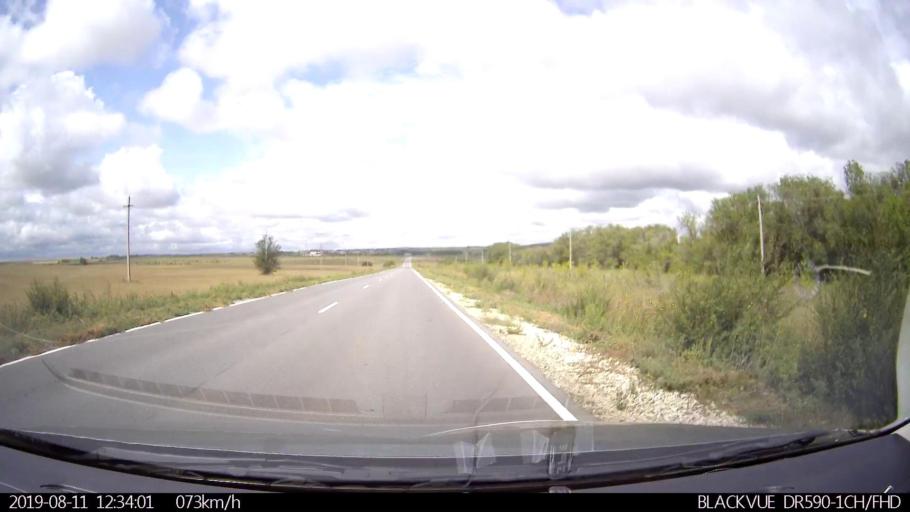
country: RU
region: Ulyanovsk
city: Ignatovka
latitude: 53.8138
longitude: 47.8483
